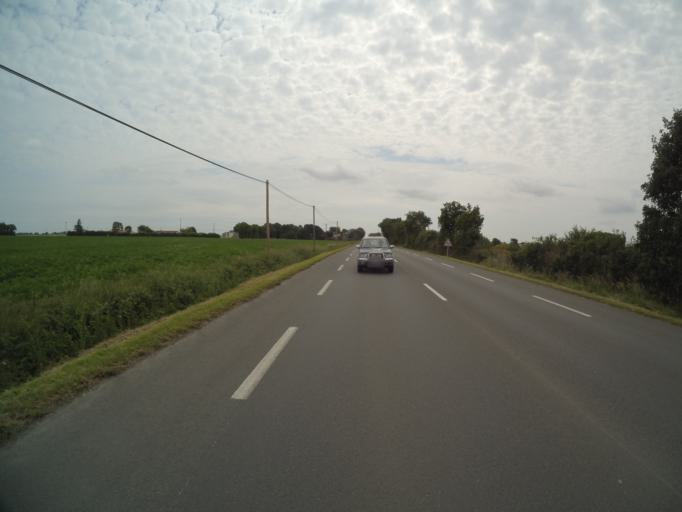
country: FR
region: Pays de la Loire
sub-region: Departement de la Vendee
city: Saint-Georges-de-Montaigu
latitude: 46.9316
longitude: -1.2670
